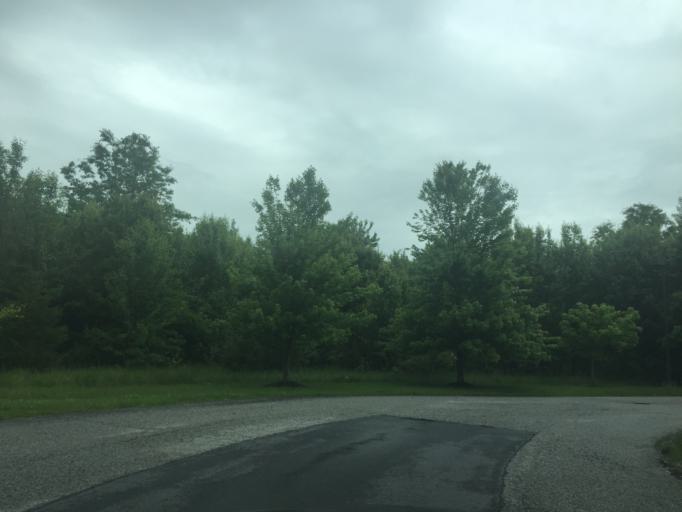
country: US
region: Maryland
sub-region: Baltimore County
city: Perry Hall
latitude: 39.4116
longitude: -76.4619
